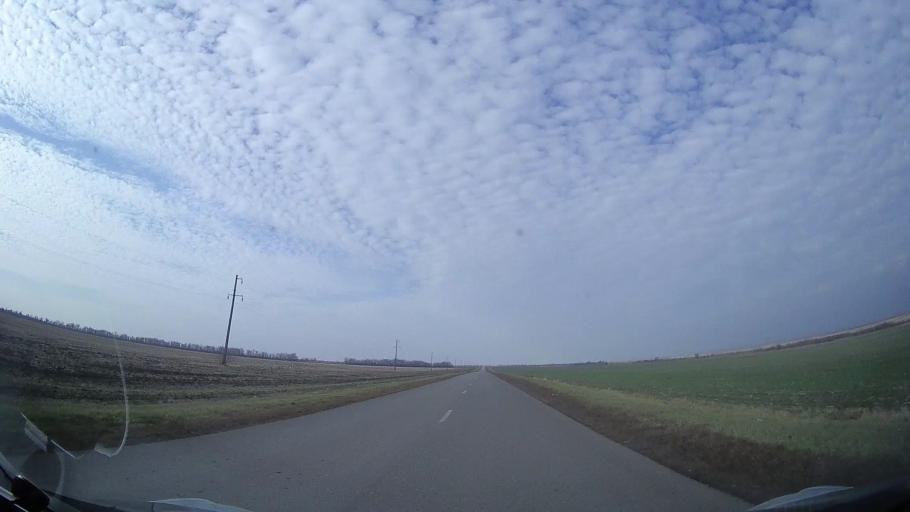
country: RU
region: Rostov
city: Veselyy
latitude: 47.0498
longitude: 40.8863
